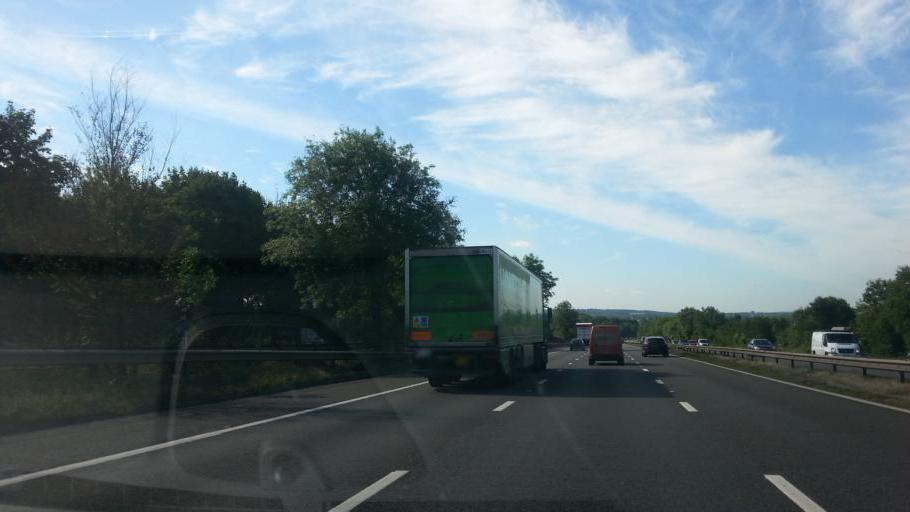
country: GB
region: England
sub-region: Hertfordshire
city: Welwyn Garden City
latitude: 51.8018
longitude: -0.2278
